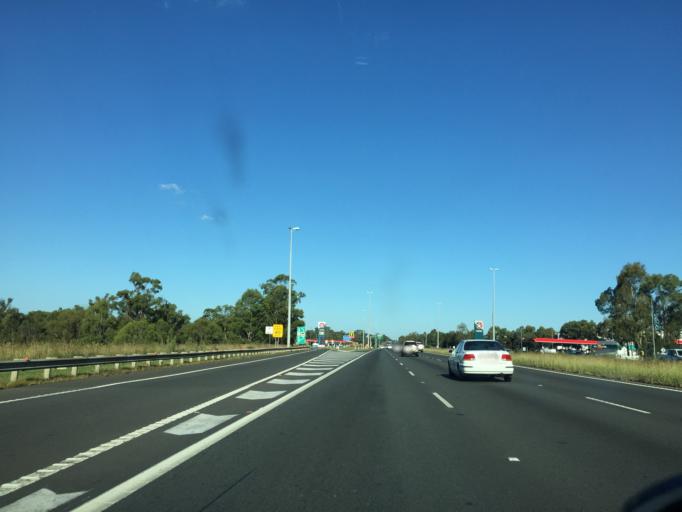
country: AU
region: New South Wales
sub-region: Blacktown
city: Doonside
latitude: -33.8017
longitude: 150.8808
